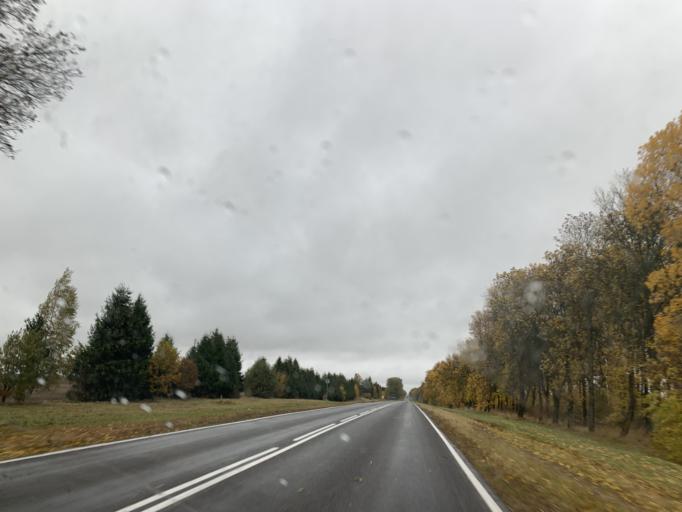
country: BY
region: Minsk
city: Novy Svyerzhan'
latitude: 53.4137
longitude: 26.6162
